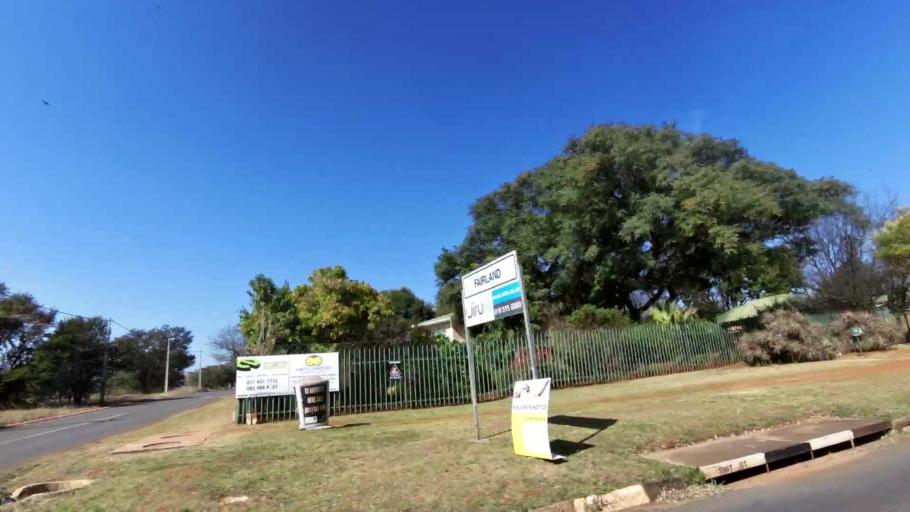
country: ZA
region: Gauteng
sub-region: City of Johannesburg Metropolitan Municipality
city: Roodepoort
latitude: -26.1223
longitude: 27.9501
